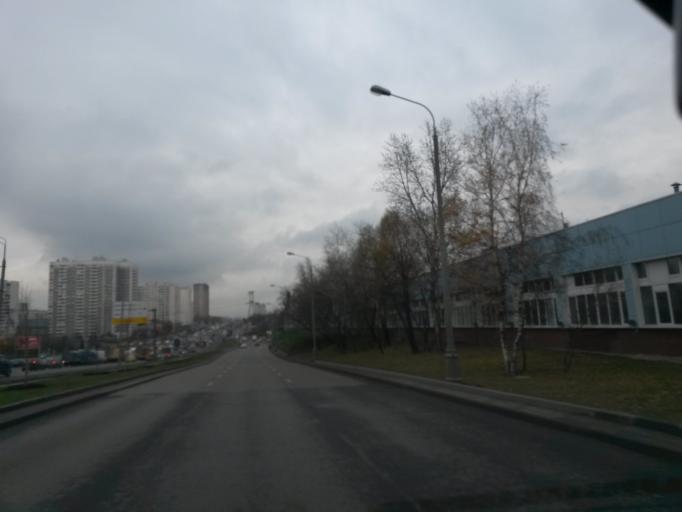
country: RU
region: Moscow
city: Nagornyy
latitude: 55.6370
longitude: 37.6204
